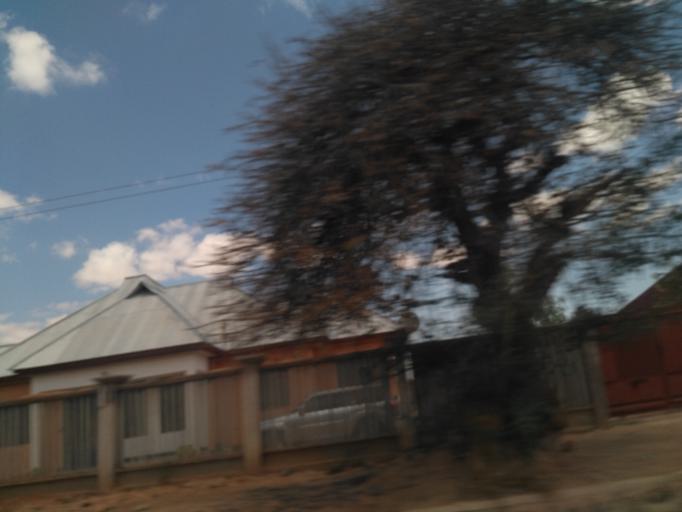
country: TZ
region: Dodoma
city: Kisasa
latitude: -6.1799
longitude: 35.7863
